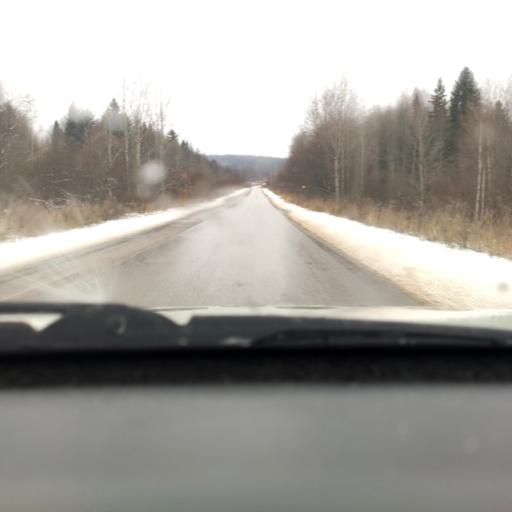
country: RU
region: Perm
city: Ferma
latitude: 57.9830
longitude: 56.3628
